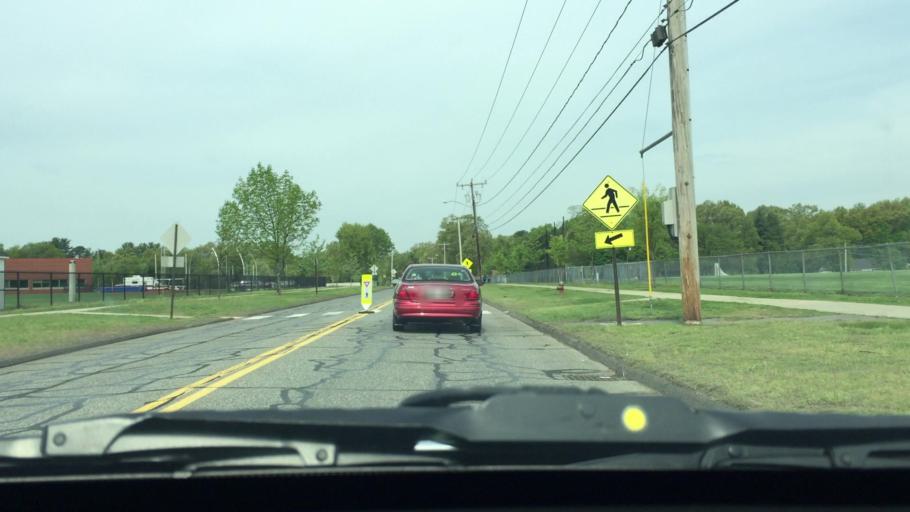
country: US
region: Massachusetts
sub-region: Hampden County
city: Longmeadow
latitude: 42.0569
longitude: -72.5583
